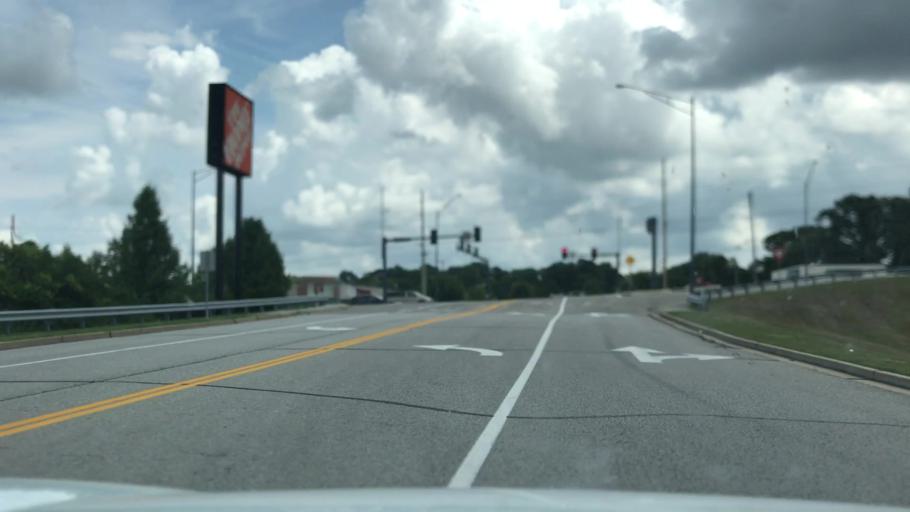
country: US
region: Missouri
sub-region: Saint Charles County
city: O'Fallon
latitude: 38.7899
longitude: -90.7004
